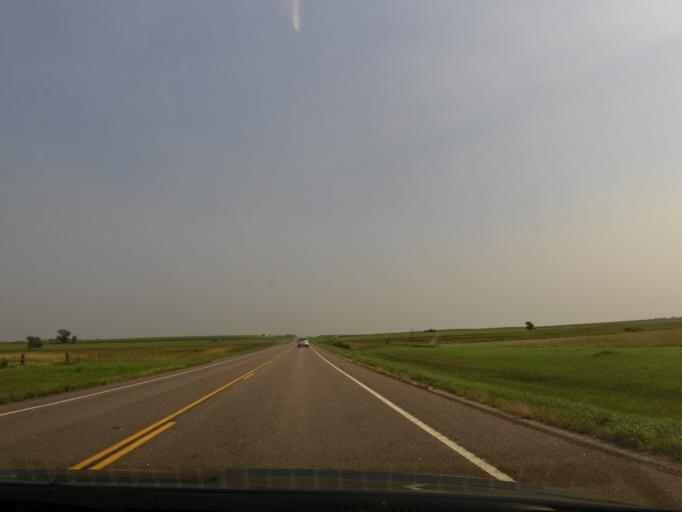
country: US
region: South Dakota
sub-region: Roberts County
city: Sisseton
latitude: 45.8486
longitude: -96.9443
